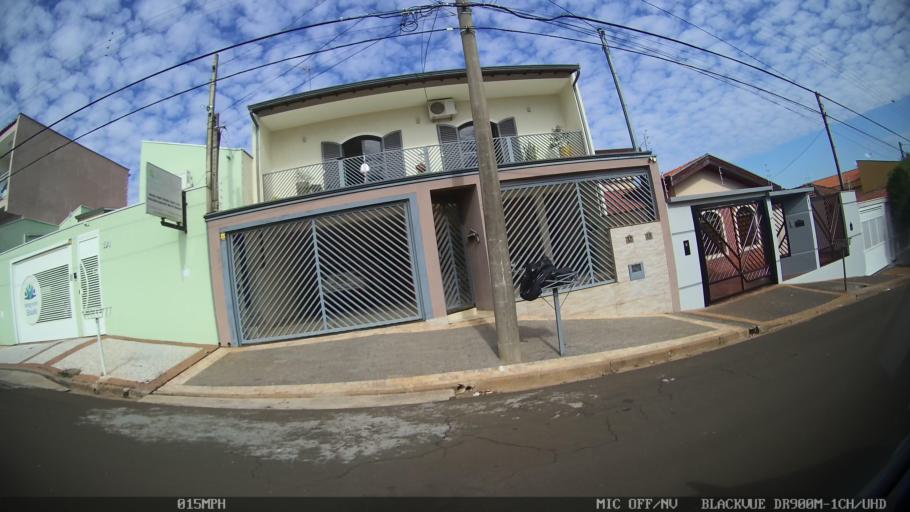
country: BR
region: Sao Paulo
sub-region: Santa Barbara D'Oeste
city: Santa Barbara d'Oeste
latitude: -22.7585
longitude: -47.4055
